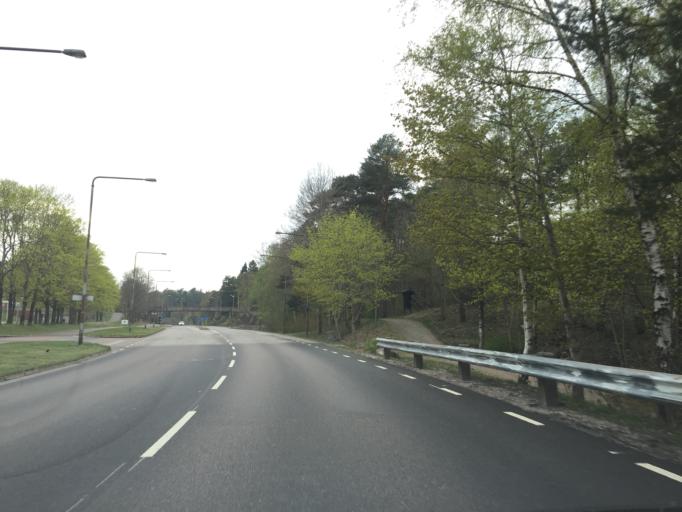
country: SE
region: Vaestra Goetaland
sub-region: Goteborg
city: Rannebergen
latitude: 57.8053
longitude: 12.0718
